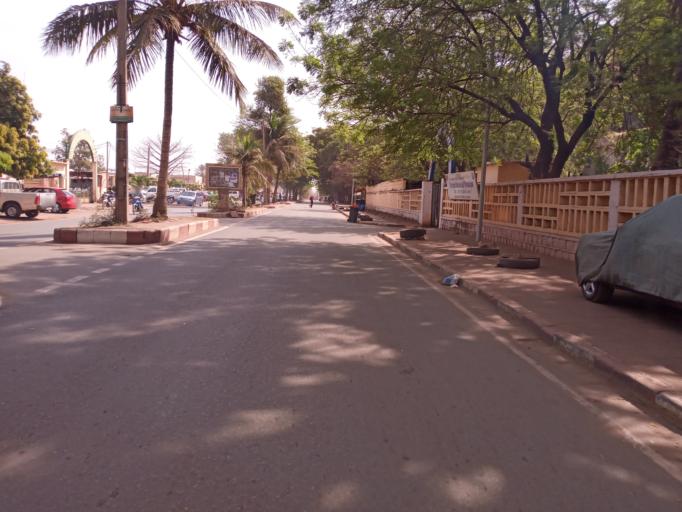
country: ML
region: Bamako
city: Bamako
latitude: 12.6385
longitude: -7.9957
